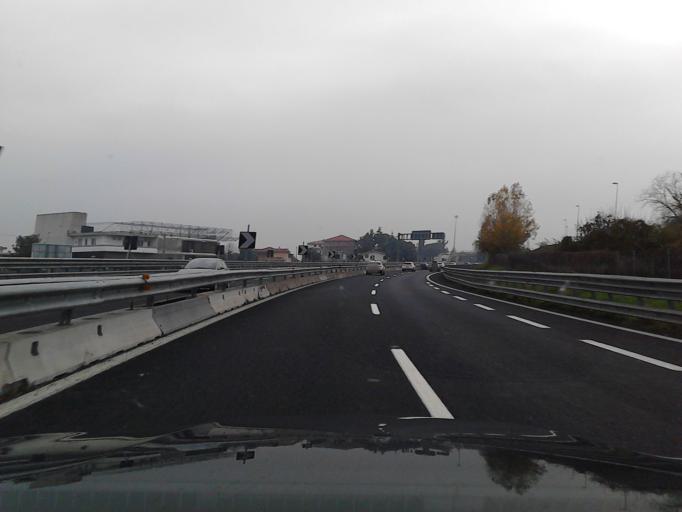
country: IT
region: Abruzzo
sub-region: Provincia di Pescara
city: San Martino Bassa
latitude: 42.5190
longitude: 14.1336
